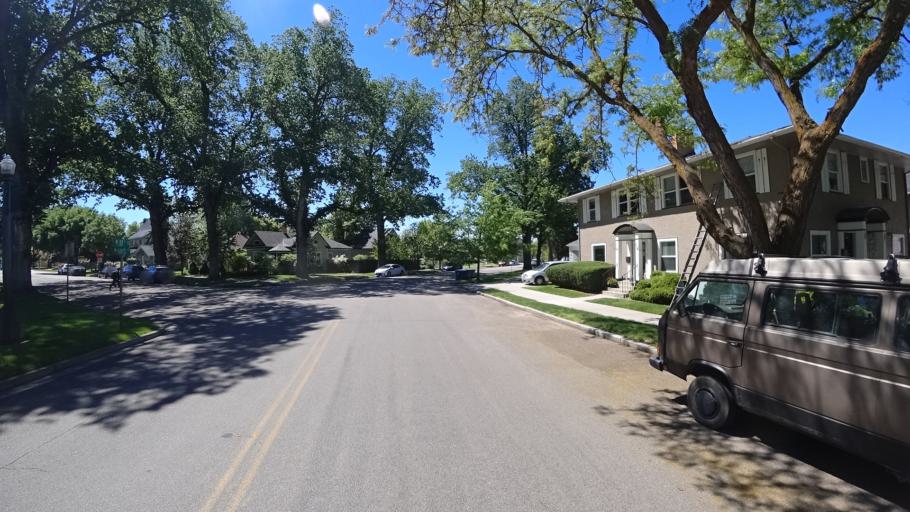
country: US
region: Idaho
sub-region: Ada County
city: Boise
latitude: 43.6265
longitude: -116.2091
